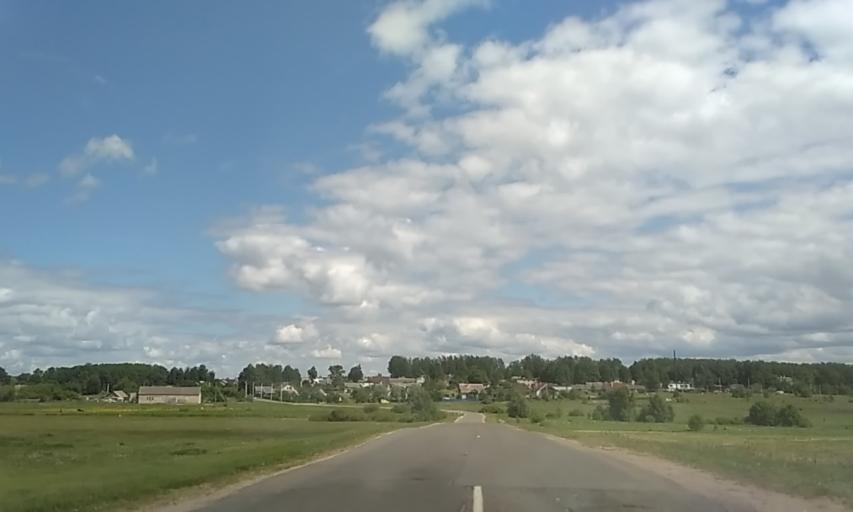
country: BY
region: Minsk
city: Krupki
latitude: 54.3618
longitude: 29.0977
